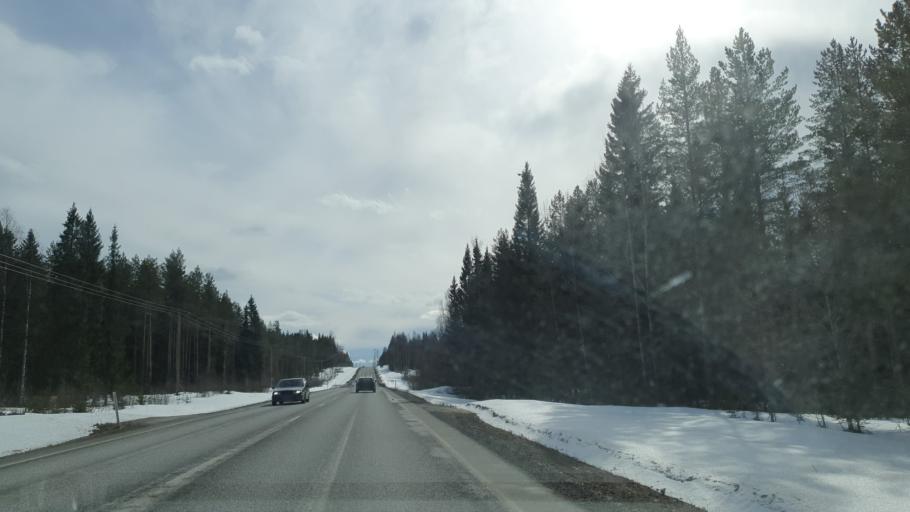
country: FI
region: Kainuu
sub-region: Kajaani
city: Ristijaervi
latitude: 64.3506
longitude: 28.0520
